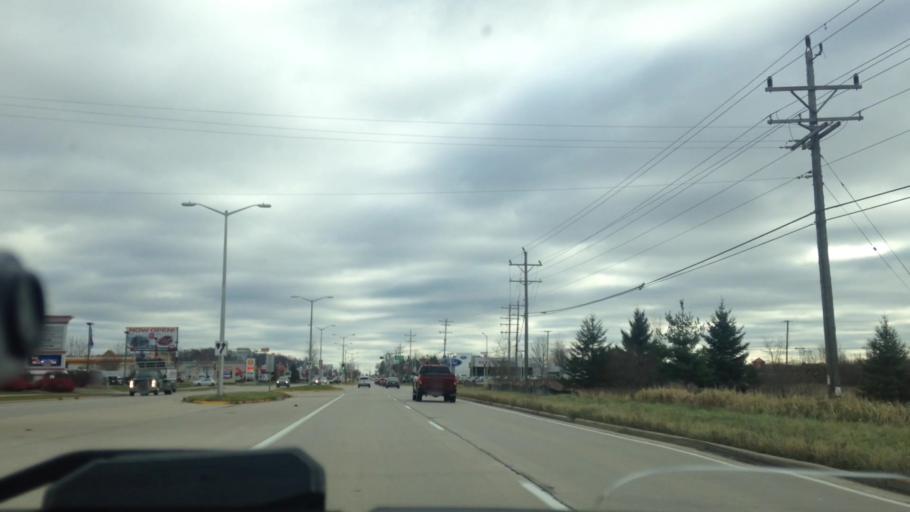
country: US
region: Wisconsin
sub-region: Washington County
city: West Bend
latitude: 43.4273
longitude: -88.2284
